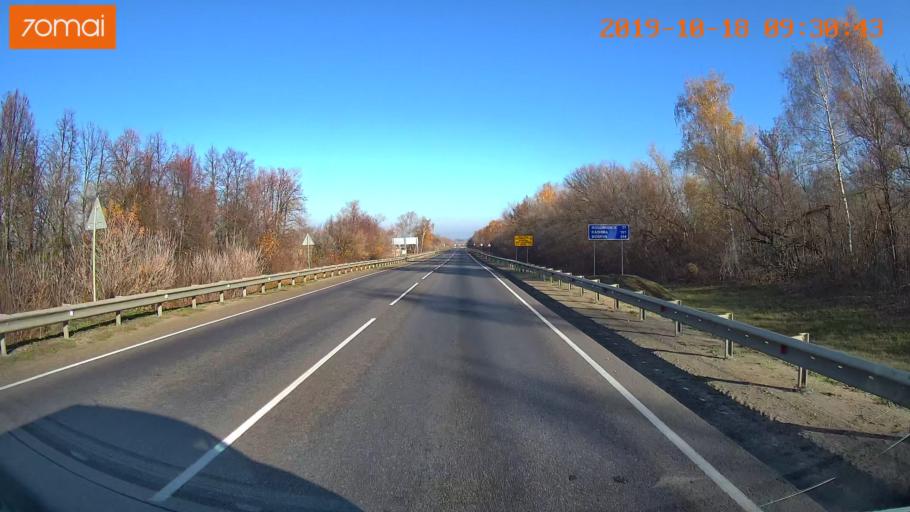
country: RU
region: Tula
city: Yefremov
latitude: 53.1415
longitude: 38.1594
